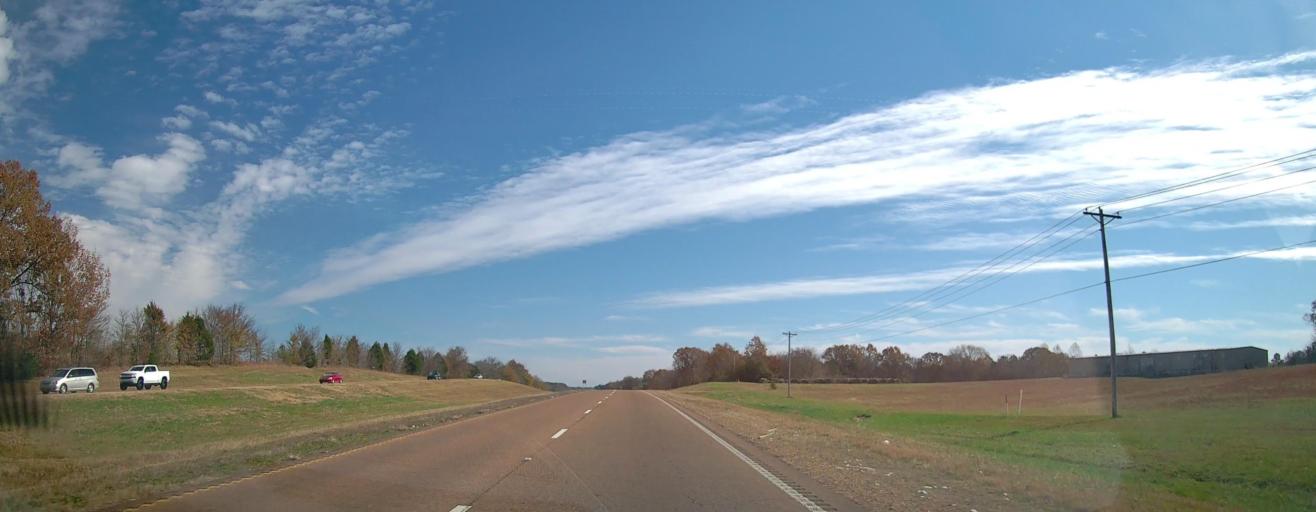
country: US
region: Tennessee
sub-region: Fayette County
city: Piperton
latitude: 34.9594
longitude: -89.5249
